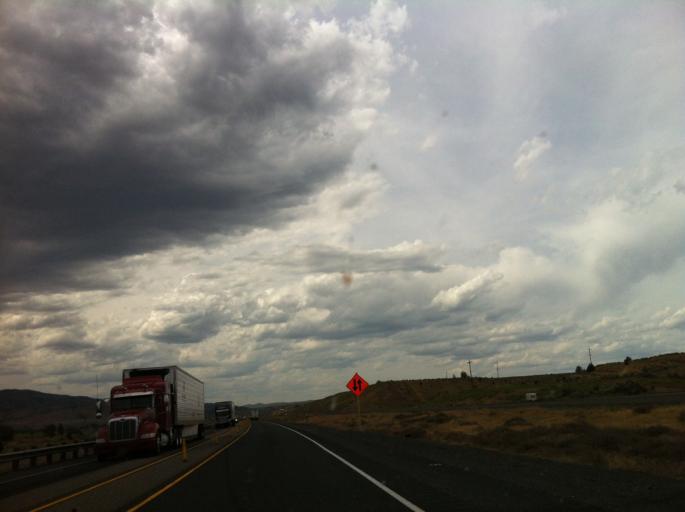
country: US
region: Oregon
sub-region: Baker County
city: Baker City
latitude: 44.5564
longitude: -117.4264
